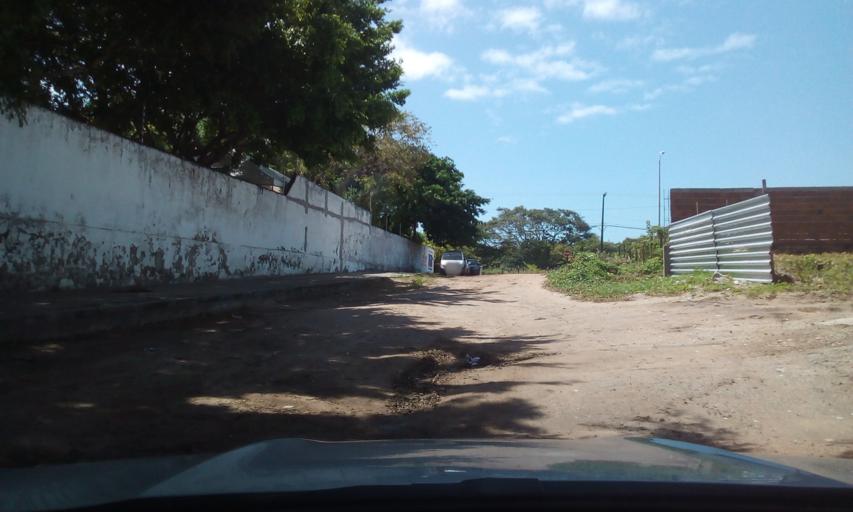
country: BR
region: Paraiba
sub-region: Joao Pessoa
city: Joao Pessoa
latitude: -7.1473
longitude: -34.8080
